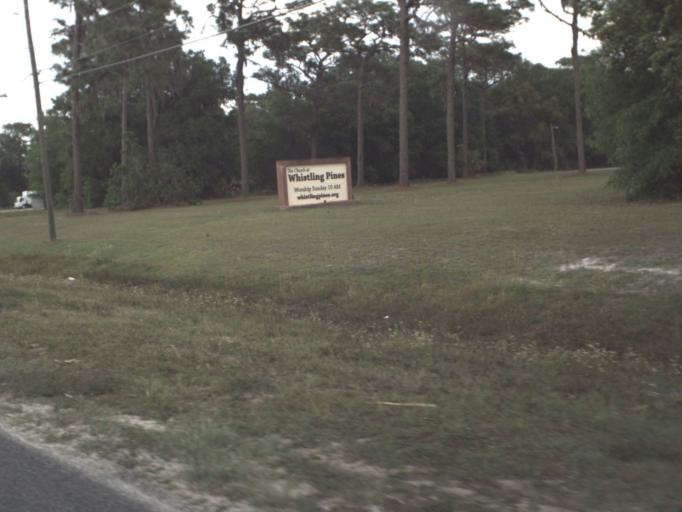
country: US
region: Florida
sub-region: Lake County
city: Umatilla
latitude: 28.8984
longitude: -81.6869
